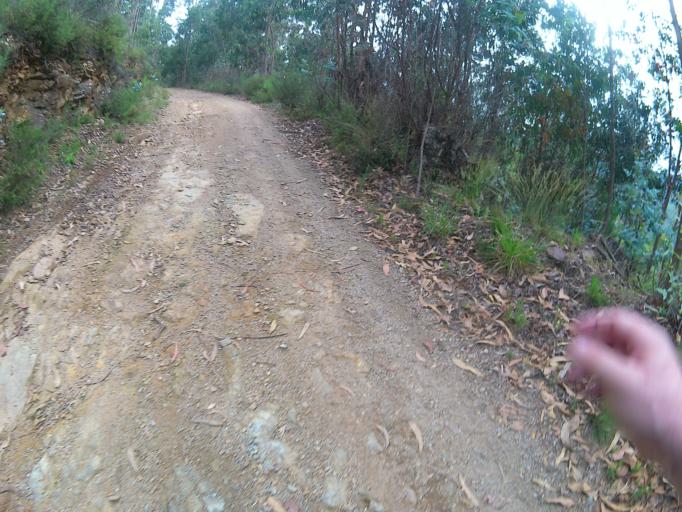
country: PT
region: Aveiro
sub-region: Albergaria-A-Velha
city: Branca
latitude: 40.7599
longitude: -8.4303
